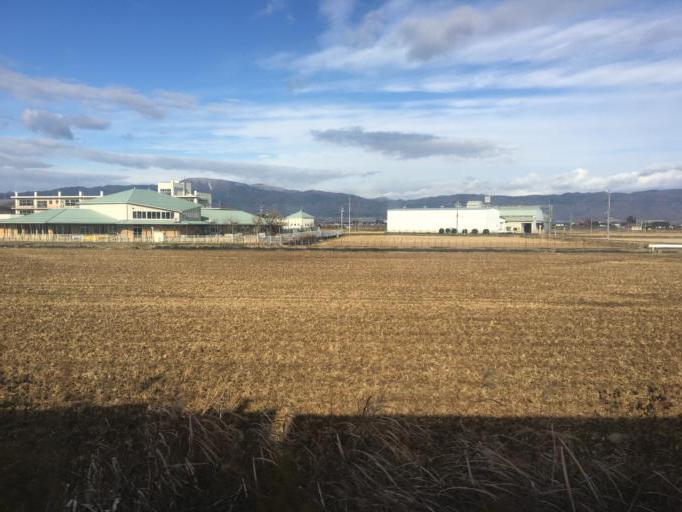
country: JP
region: Fukushima
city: Hobaramachi
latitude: 37.8248
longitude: 140.5759
